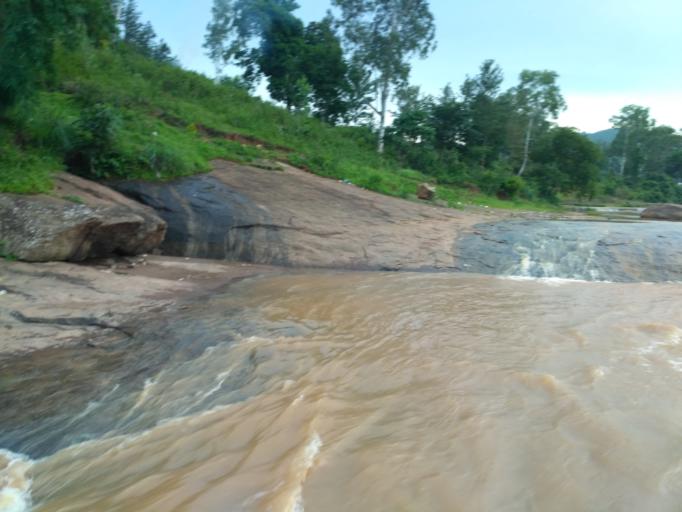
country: IN
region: Andhra Pradesh
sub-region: Vishakhapatnam
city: Madugula
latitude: 18.2919
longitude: 82.7982
